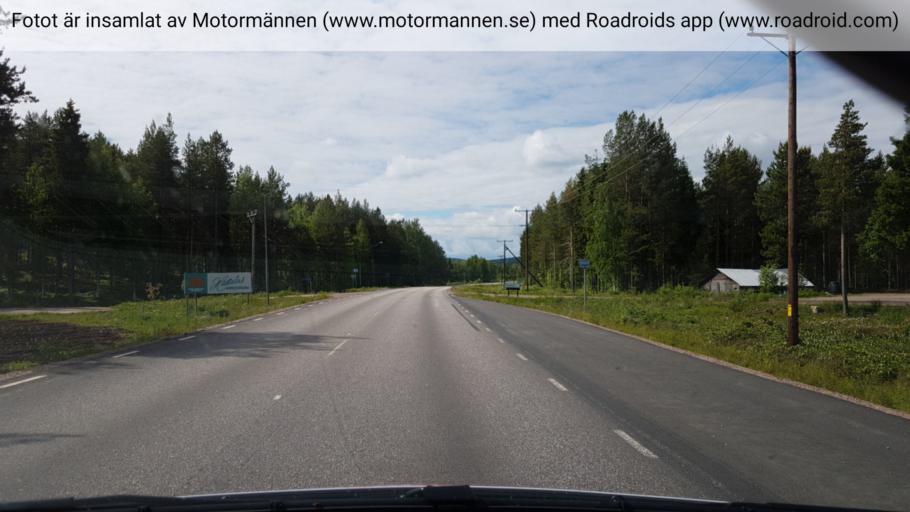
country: SE
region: Norrbotten
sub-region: Overtornea Kommun
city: OEvertornea
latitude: 66.4702
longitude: 23.6700
